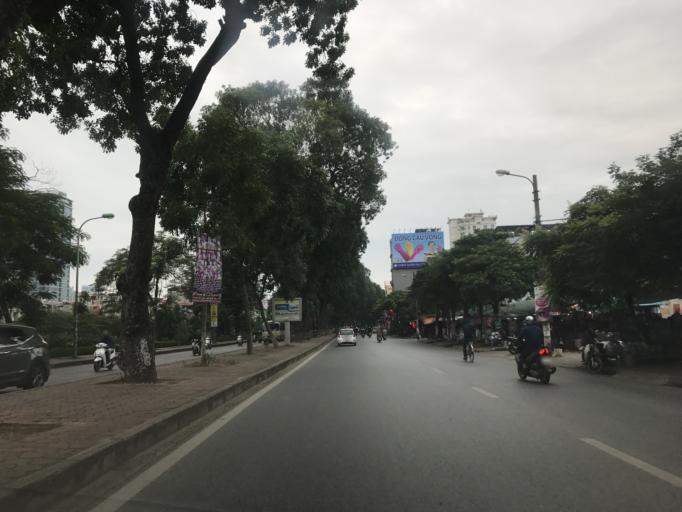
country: VN
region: Ha Noi
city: Thanh Xuan
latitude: 21.0131
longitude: 105.8079
